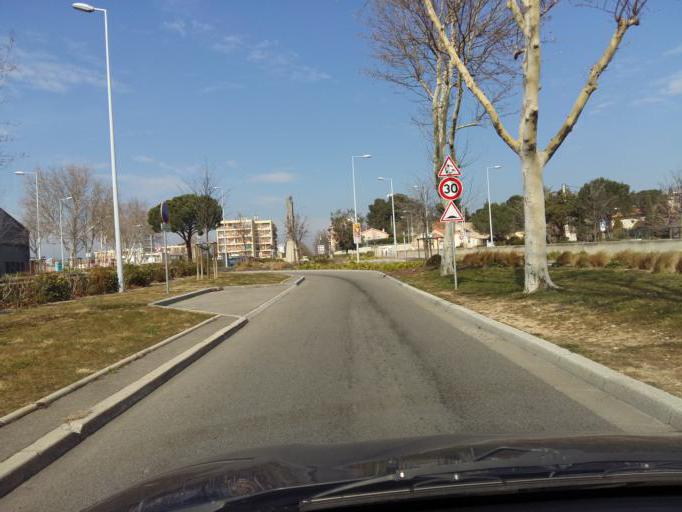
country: FR
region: Provence-Alpes-Cote d'Azur
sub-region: Departement des Bouches-du-Rhone
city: Salon-de-Provence
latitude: 43.6306
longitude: 5.1015
